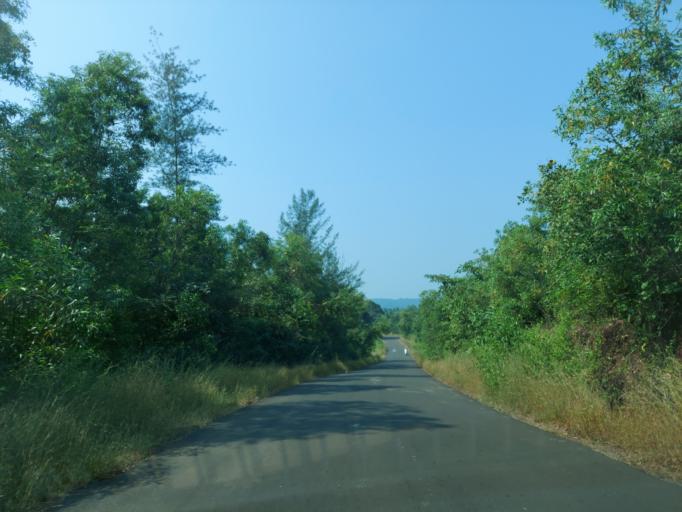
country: IN
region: Maharashtra
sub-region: Sindhudurg
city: Kudal
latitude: 15.9716
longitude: 73.6452
